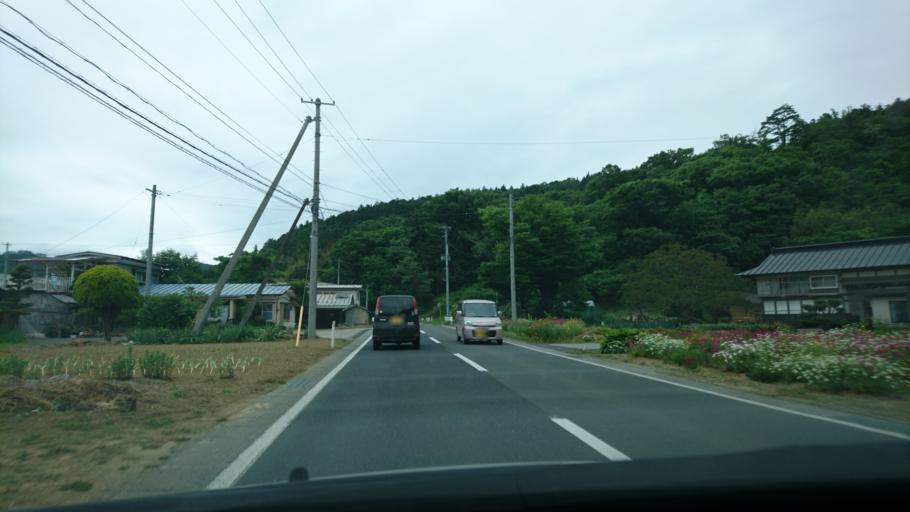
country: JP
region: Iwate
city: Ichinoseki
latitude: 38.9611
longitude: 141.2515
